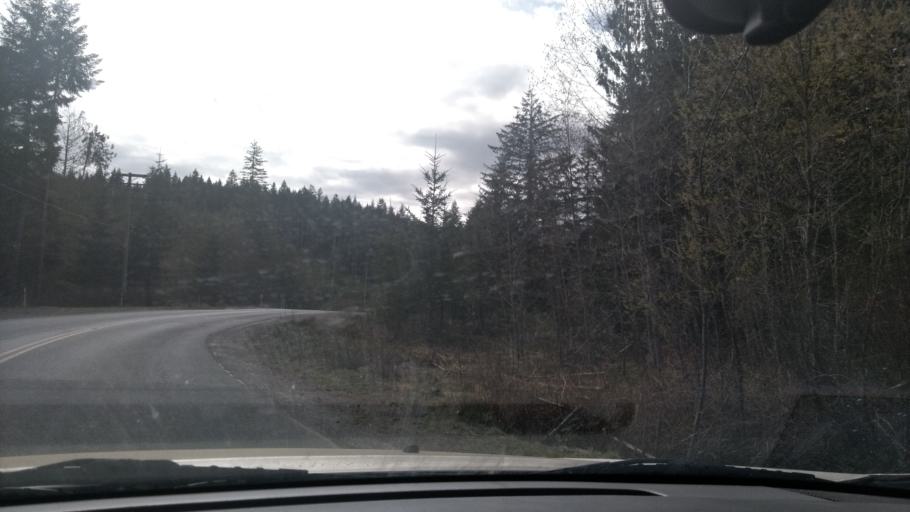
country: CA
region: British Columbia
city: Campbell River
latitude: 49.9857
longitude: -125.4230
